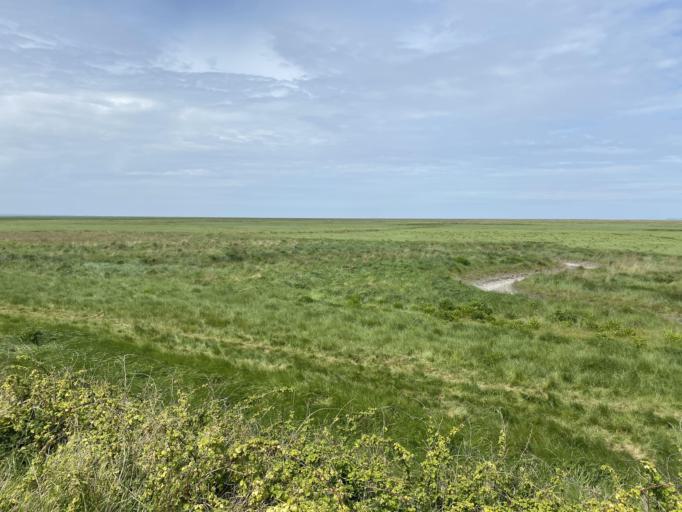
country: FR
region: Brittany
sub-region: Departement d'Ille-et-Vilaine
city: Roz-sur-Couesnon
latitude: 48.6294
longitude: -1.5531
